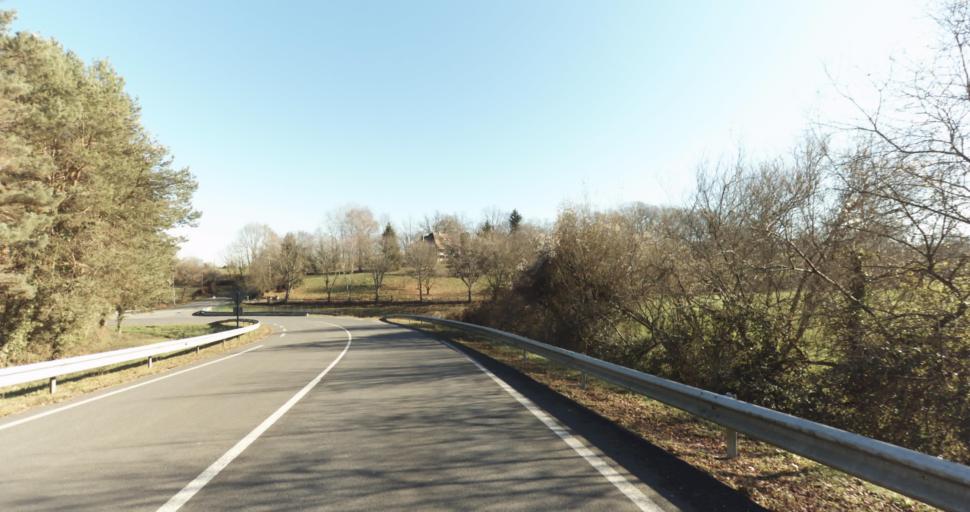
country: FR
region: Aquitaine
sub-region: Departement des Pyrenees-Atlantiques
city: Morlaas
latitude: 43.3366
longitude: -0.2685
